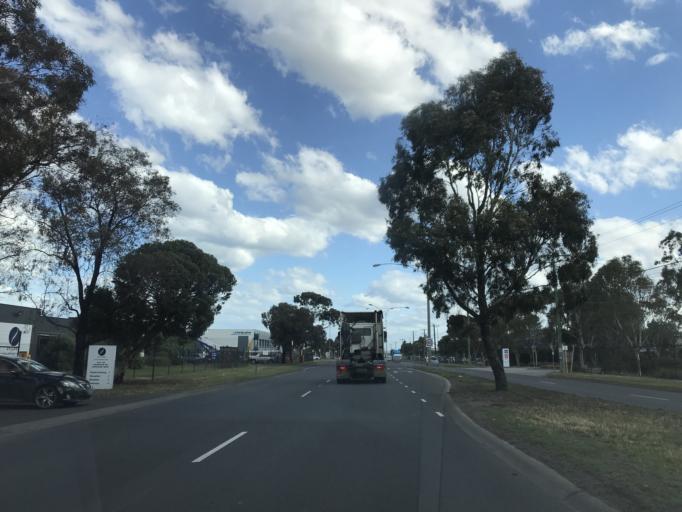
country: AU
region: Victoria
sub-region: Brimbank
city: Sunshine West
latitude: -37.8091
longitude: 144.8182
